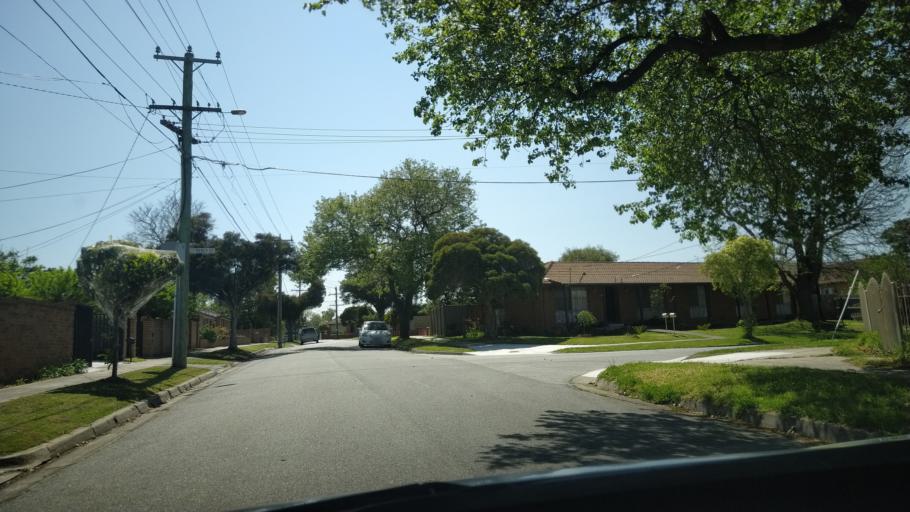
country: AU
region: Victoria
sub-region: Greater Dandenong
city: Noble Park
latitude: -37.9686
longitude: 145.1635
